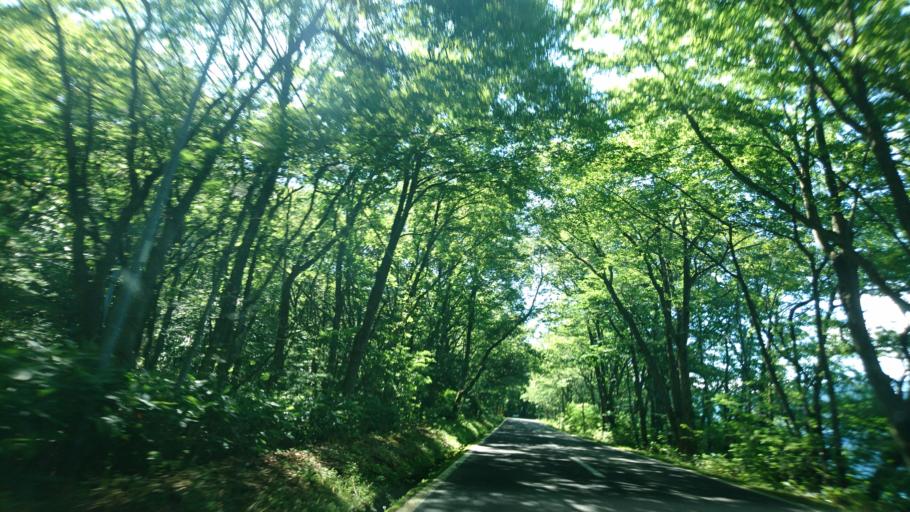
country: JP
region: Akita
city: Kakunodatemachi
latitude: 39.7463
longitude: 140.6812
